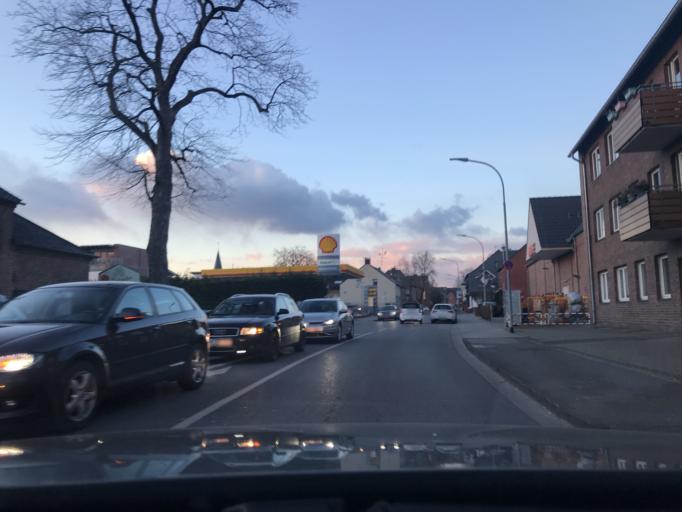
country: DE
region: North Rhine-Westphalia
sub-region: Regierungsbezirk Dusseldorf
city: Kaarst
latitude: 51.2321
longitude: 6.6180
